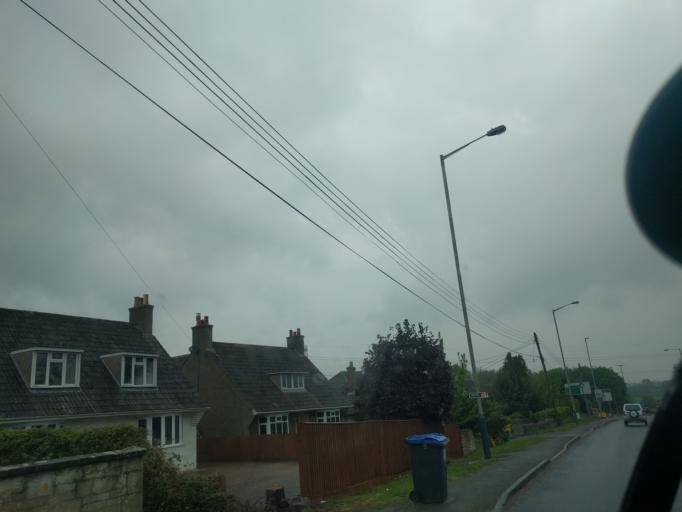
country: GB
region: England
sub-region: Wiltshire
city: Chippenham
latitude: 51.4768
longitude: -2.1276
